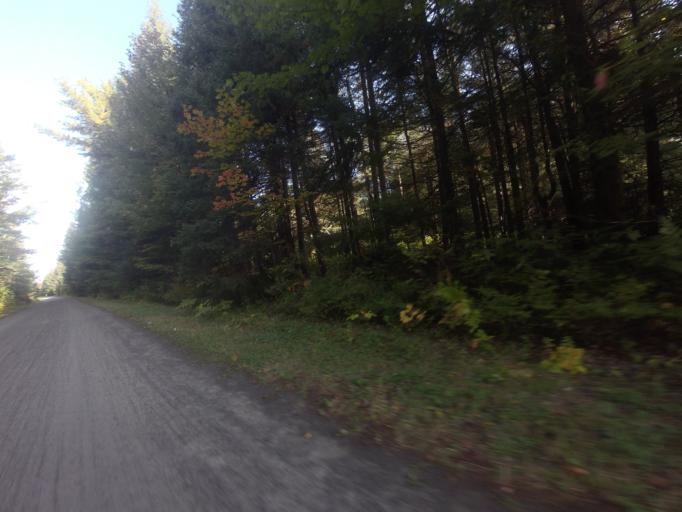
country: CA
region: Quebec
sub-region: Laurentides
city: Val-David
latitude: 46.0218
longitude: -74.1922
